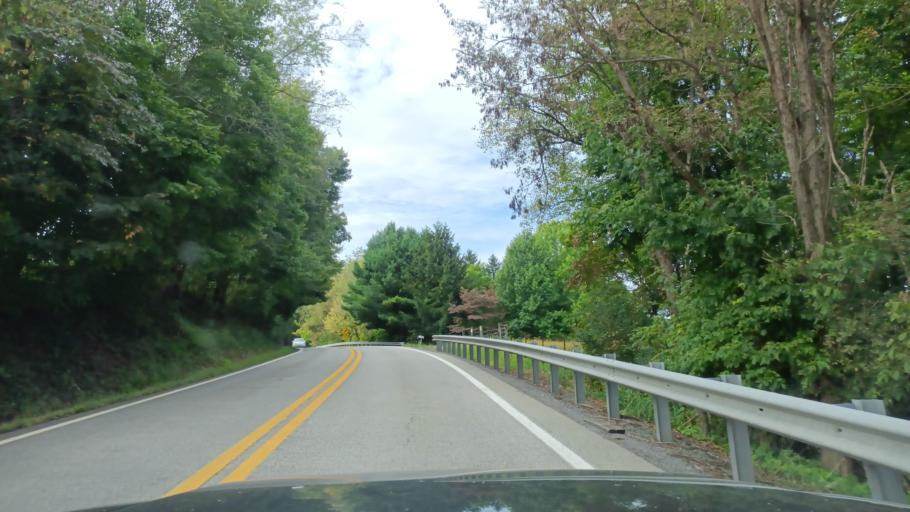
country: US
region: West Virginia
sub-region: Harrison County
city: Bridgeport
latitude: 39.3135
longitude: -80.1405
